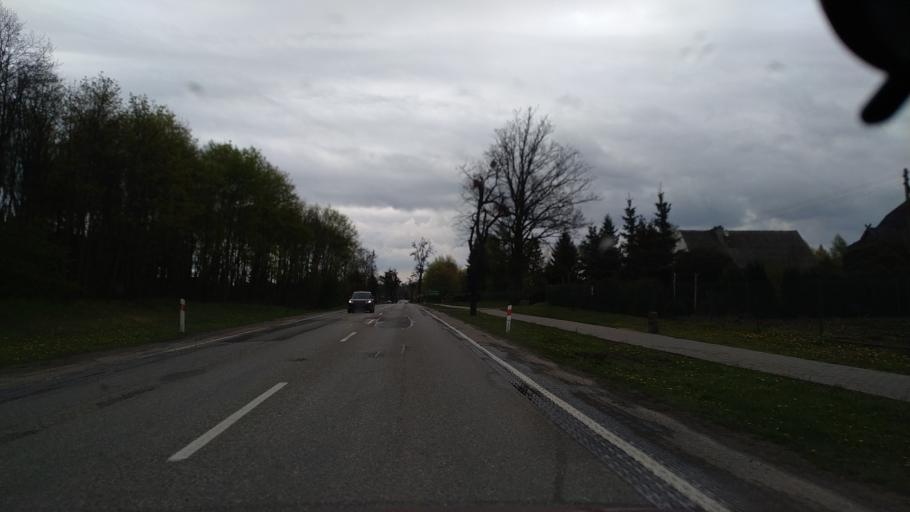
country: PL
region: Pomeranian Voivodeship
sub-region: Powiat tczewski
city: Pelplin
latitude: 54.0310
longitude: 18.6498
